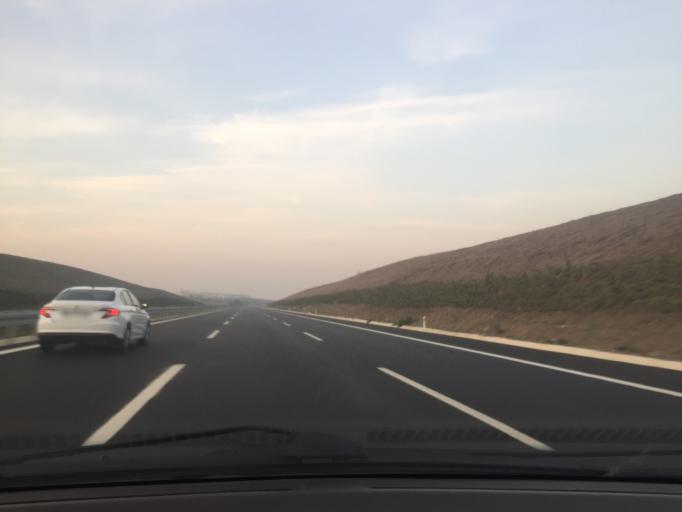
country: TR
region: Bursa
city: Karacabey
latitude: 40.2631
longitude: 28.4867
